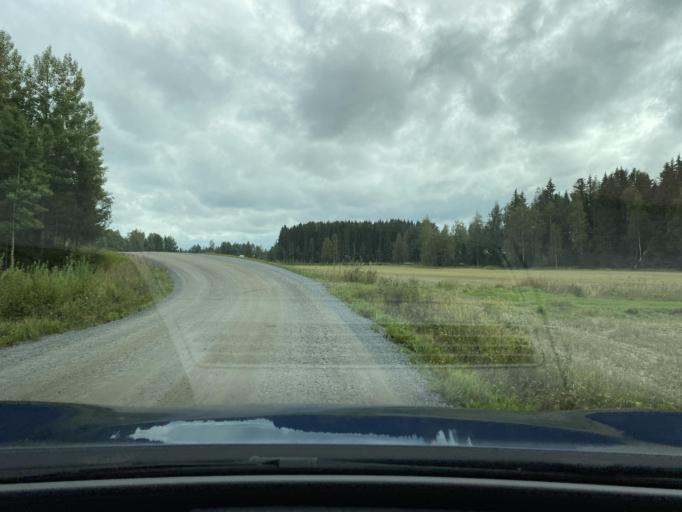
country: FI
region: Pirkanmaa
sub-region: Lounais-Pirkanmaa
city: Vammala
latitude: 61.2634
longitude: 23.0054
